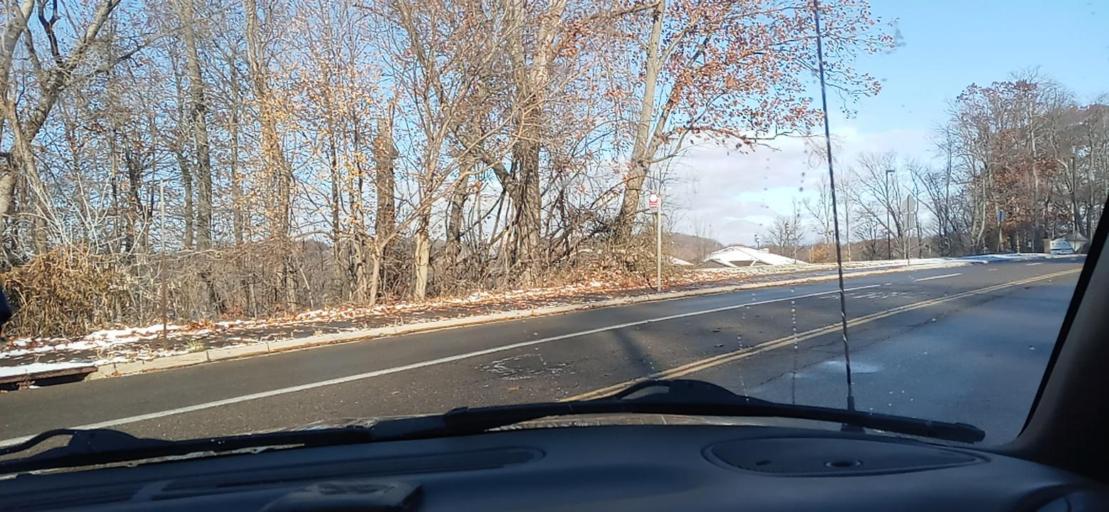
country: US
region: Ohio
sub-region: Summit County
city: Akron
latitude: 41.0580
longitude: -81.5404
